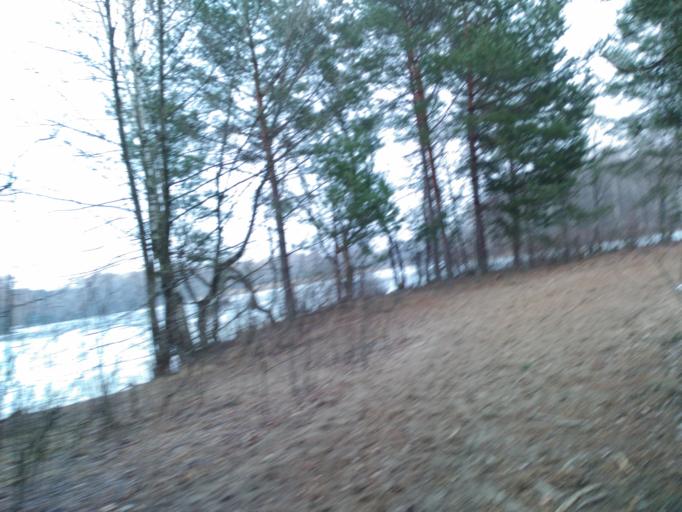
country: RU
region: Moscow
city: Shchukino
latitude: 55.7775
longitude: 37.4246
